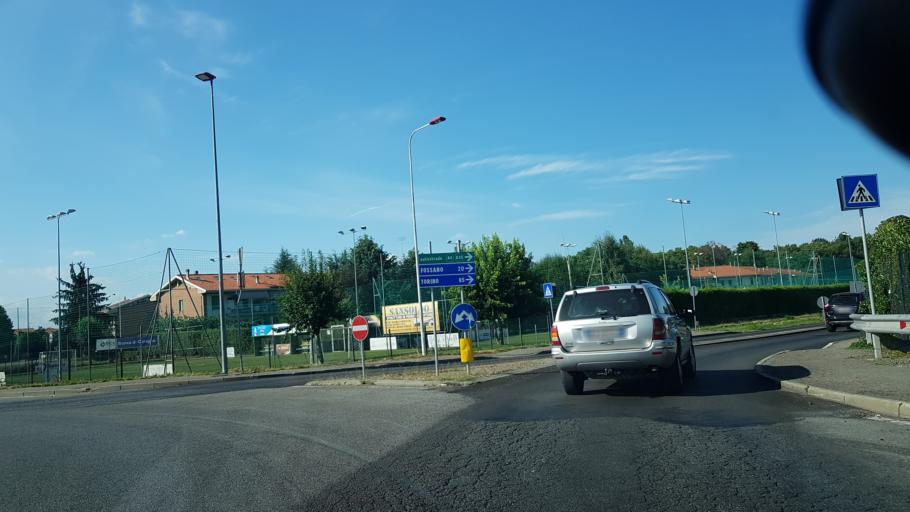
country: IT
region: Piedmont
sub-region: Provincia di Cuneo
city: Cuneo
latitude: 44.4070
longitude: 7.5493
